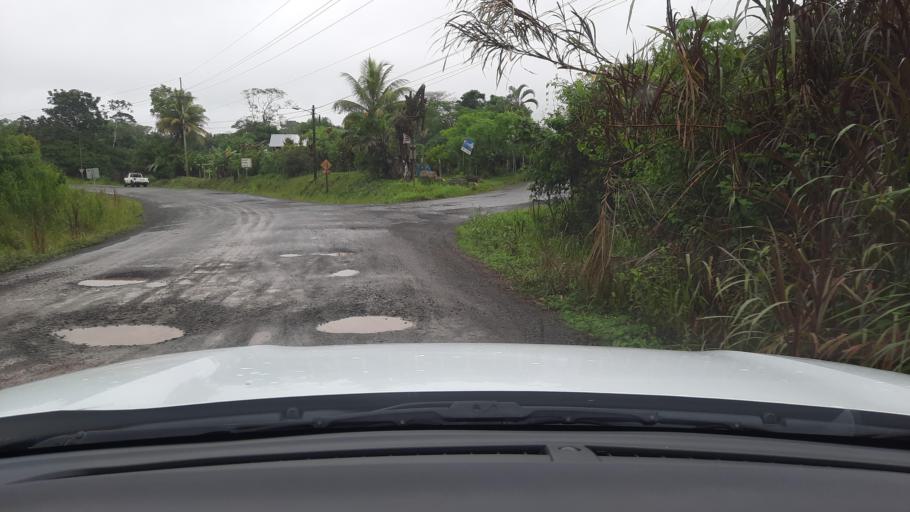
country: CR
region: Alajuela
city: San Jose
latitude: 11.0119
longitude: -85.3503
